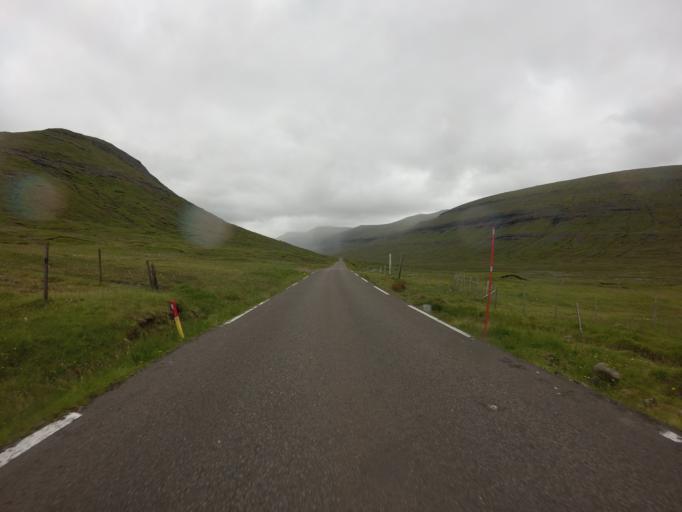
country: FO
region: Streymoy
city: Vestmanna
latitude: 62.2090
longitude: -7.1115
